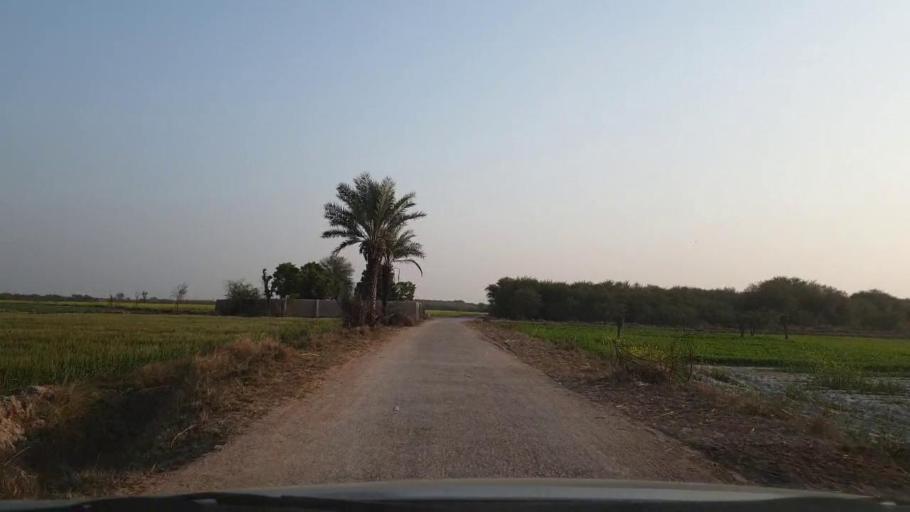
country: PK
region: Sindh
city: Tando Adam
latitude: 25.7176
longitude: 68.5940
